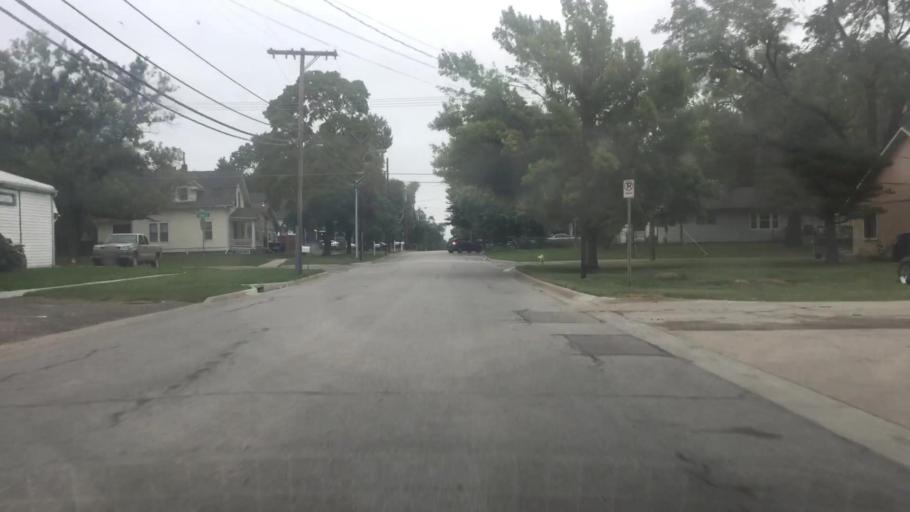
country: US
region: Kansas
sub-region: Douglas County
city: Lawrence
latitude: 38.9746
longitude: -95.2511
